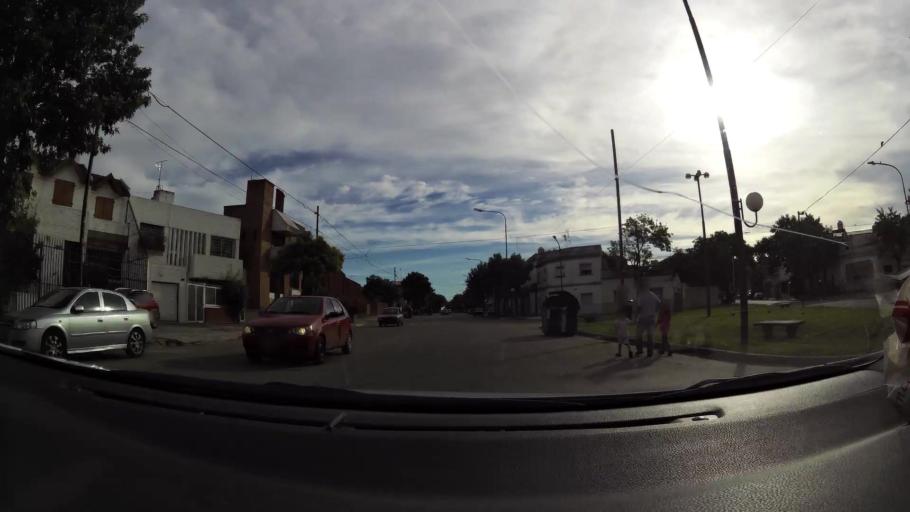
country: AR
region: Buenos Aires F.D.
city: Villa Santa Rita
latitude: -34.6402
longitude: -58.4413
